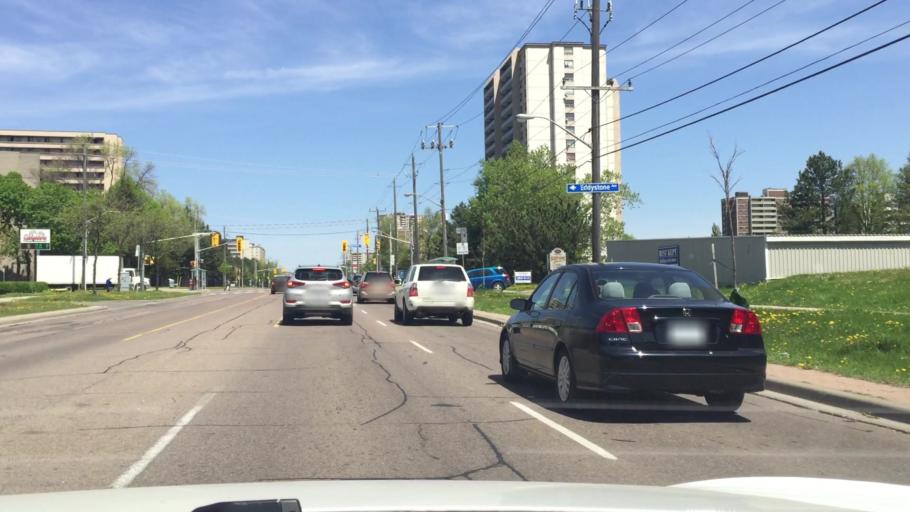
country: CA
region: Ontario
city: Concord
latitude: 43.7482
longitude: -79.5154
